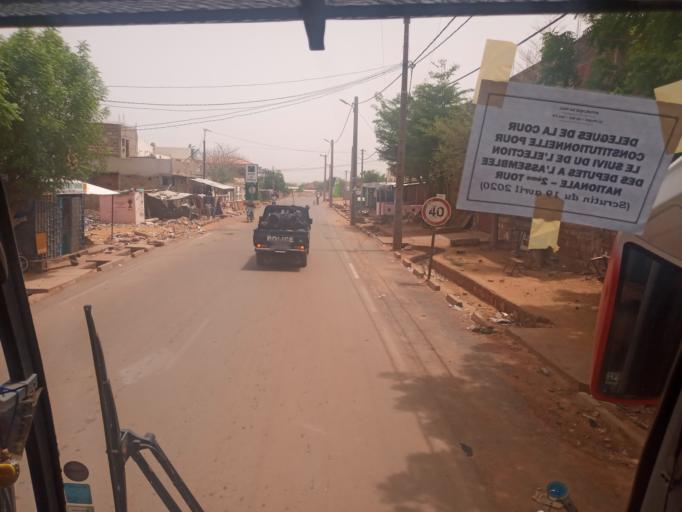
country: ML
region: Koulikoro
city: Koulikoro
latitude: 12.8648
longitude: -7.5572
